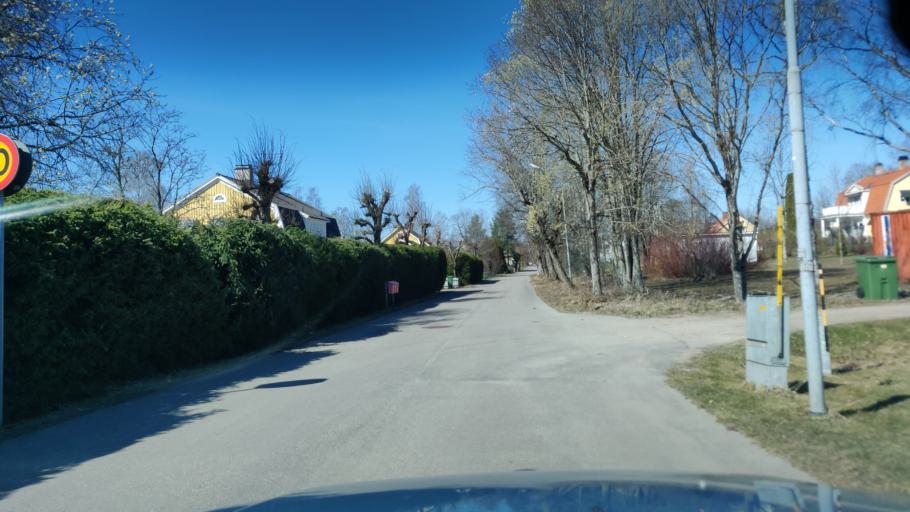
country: SE
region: Vaermland
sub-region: Hagfors Kommun
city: Hagfors
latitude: 60.0344
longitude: 13.6859
